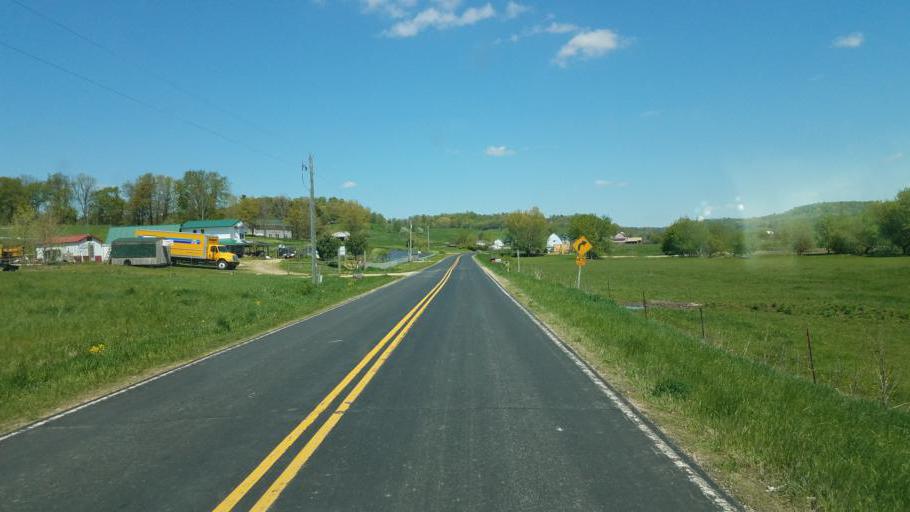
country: US
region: Wisconsin
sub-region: Vernon County
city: Hillsboro
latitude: 43.5659
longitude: -90.4426
